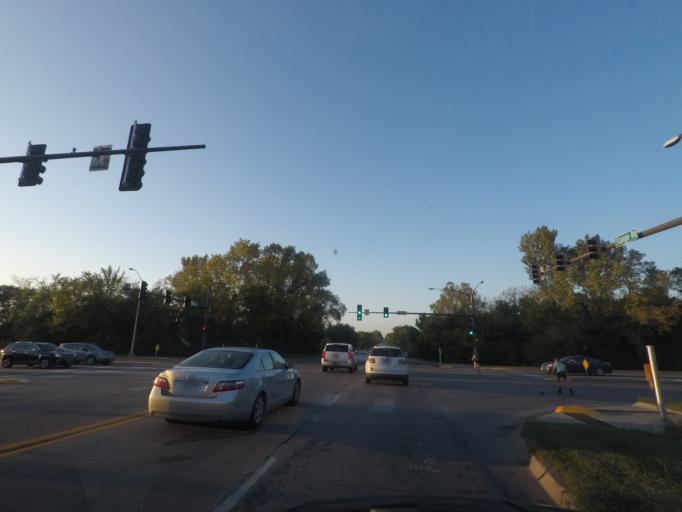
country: US
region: Iowa
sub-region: Story County
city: Ames
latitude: 42.0354
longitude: -93.6447
